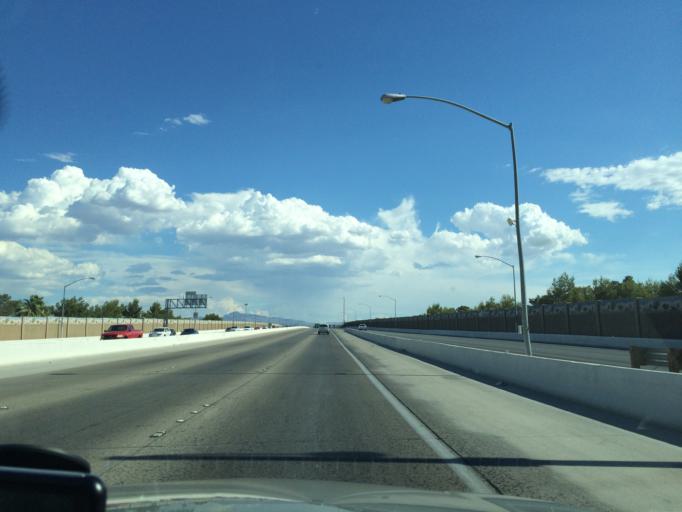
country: US
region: Nevada
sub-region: Clark County
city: Winchester
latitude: 36.1558
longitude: -115.0917
